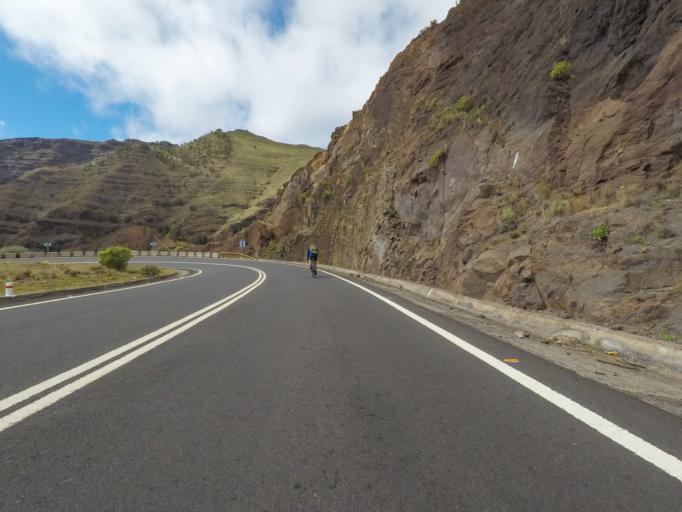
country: ES
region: Canary Islands
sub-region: Provincia de Santa Cruz de Tenerife
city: Vallehermosa
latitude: 28.1180
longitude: -17.3221
